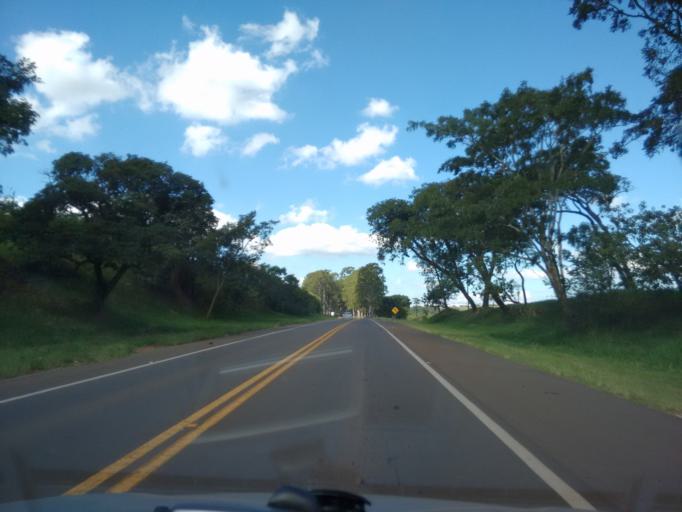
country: BR
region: Sao Paulo
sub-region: Sao Carlos
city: Sao Carlos
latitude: -22.0670
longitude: -47.9064
